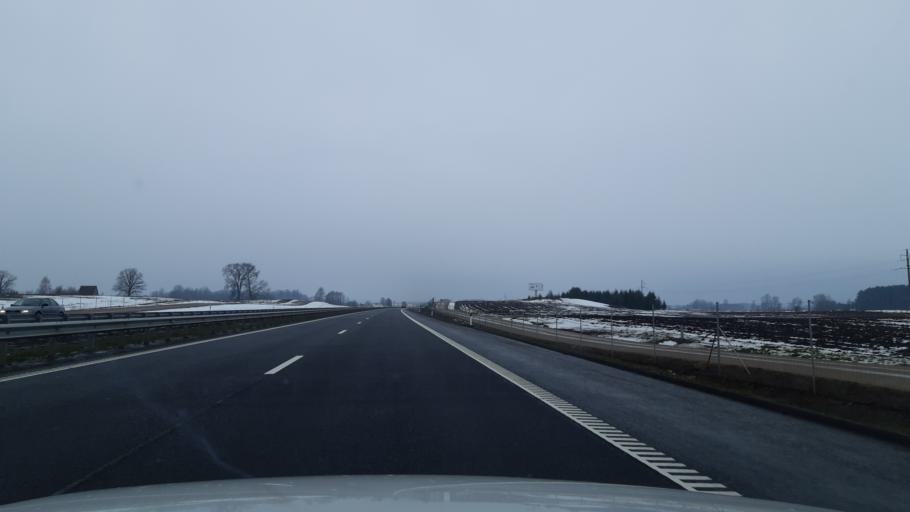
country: LT
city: Kazlu Ruda
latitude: 54.7190
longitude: 23.6641
